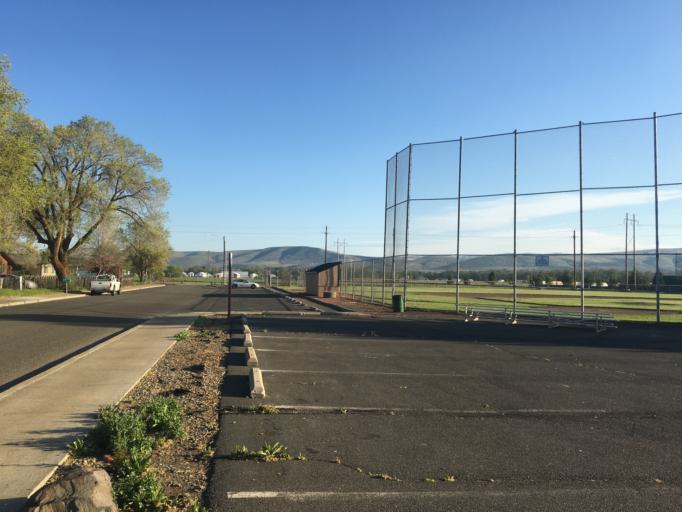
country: US
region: Washington
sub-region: Kittitas County
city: Ellensburg
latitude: 46.9930
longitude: -120.5600
